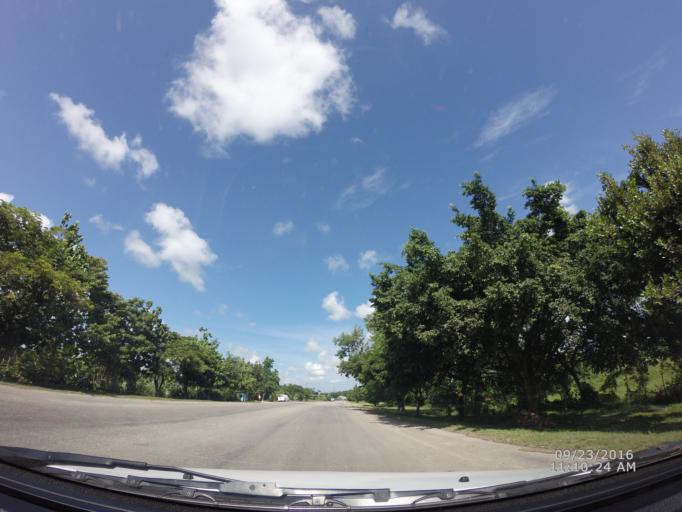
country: CU
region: La Habana
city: Arroyo Naranjo
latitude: 23.0203
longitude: -82.2558
